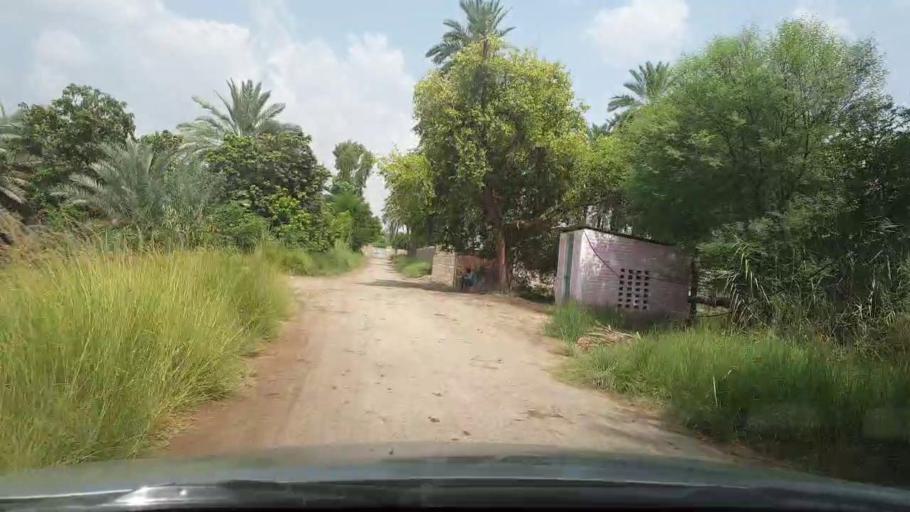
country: PK
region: Sindh
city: Khairpur
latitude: 27.4677
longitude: 68.7747
